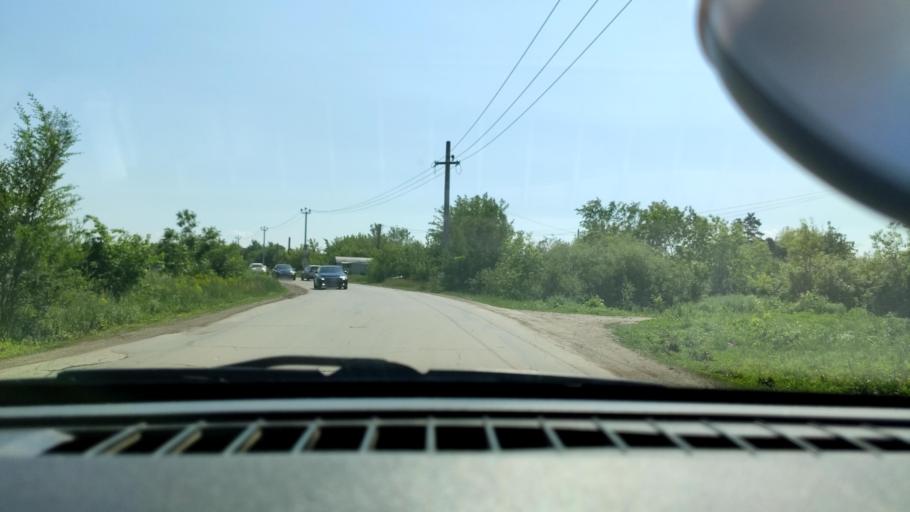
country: RU
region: Samara
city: Novokuybyshevsk
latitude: 53.0733
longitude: 50.0664
